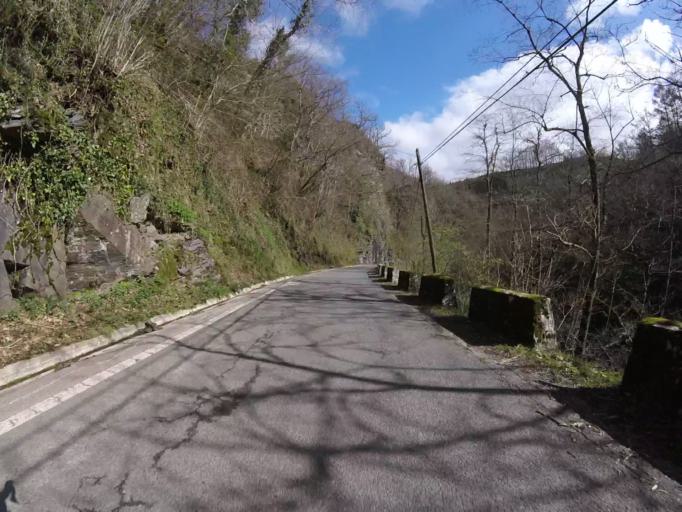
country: ES
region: Navarre
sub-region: Provincia de Navarra
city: Goizueta
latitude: 43.1394
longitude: -1.8478
